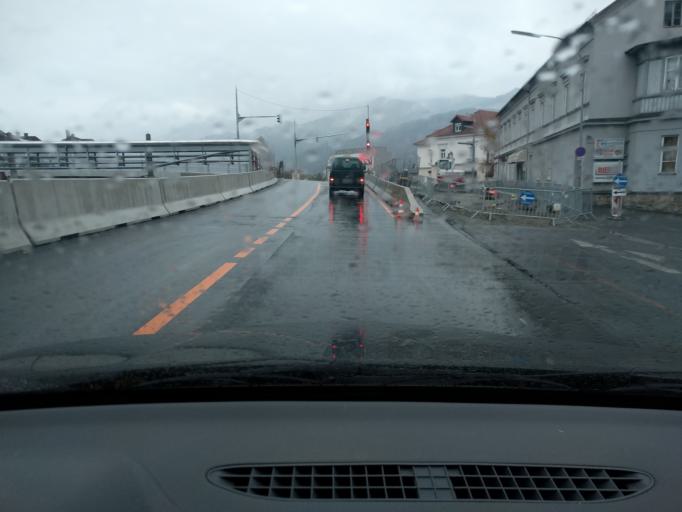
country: AT
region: Styria
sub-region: Politischer Bezirk Leoben
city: Leoben
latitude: 47.3877
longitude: 15.0999
